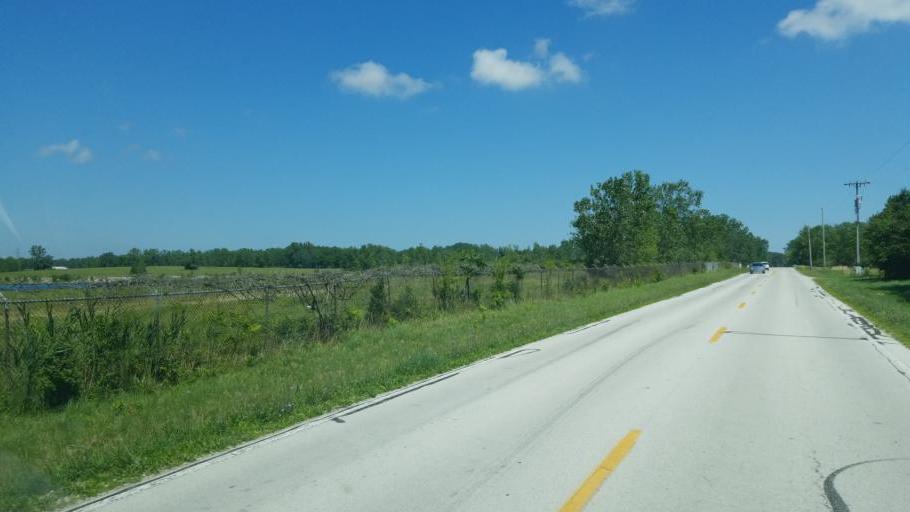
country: US
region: Ohio
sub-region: Ottawa County
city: Port Clinton
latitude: 41.4940
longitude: -82.8979
